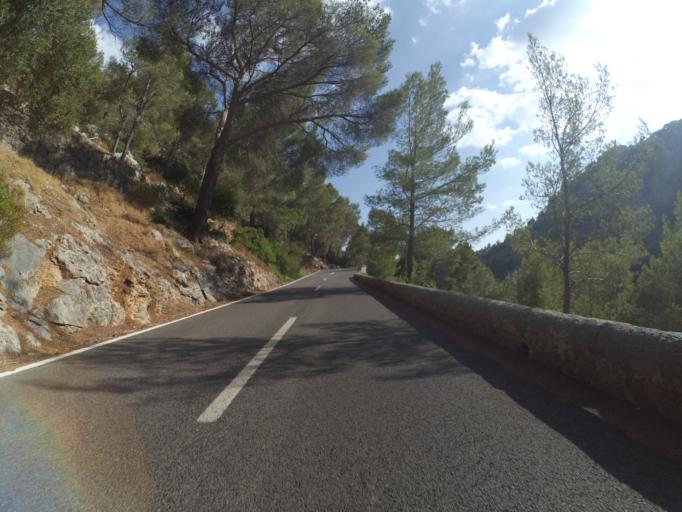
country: ES
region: Balearic Islands
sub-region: Illes Balears
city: Selva
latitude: 39.7756
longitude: 2.8982
